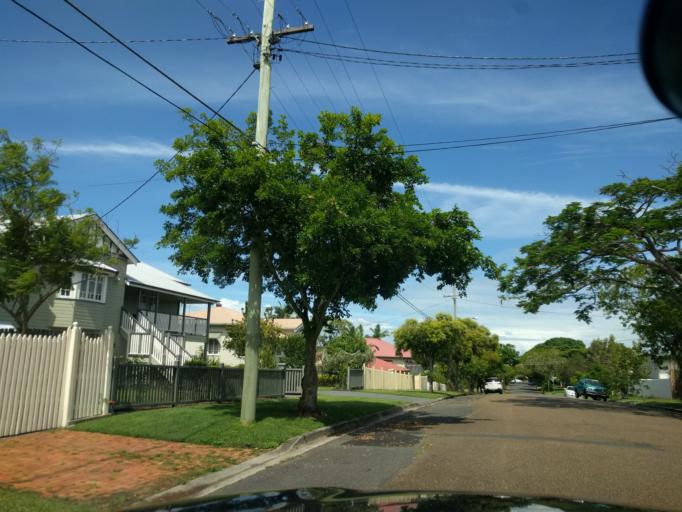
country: AU
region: Queensland
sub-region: Brisbane
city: Wilston
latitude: -27.4381
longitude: 153.0188
